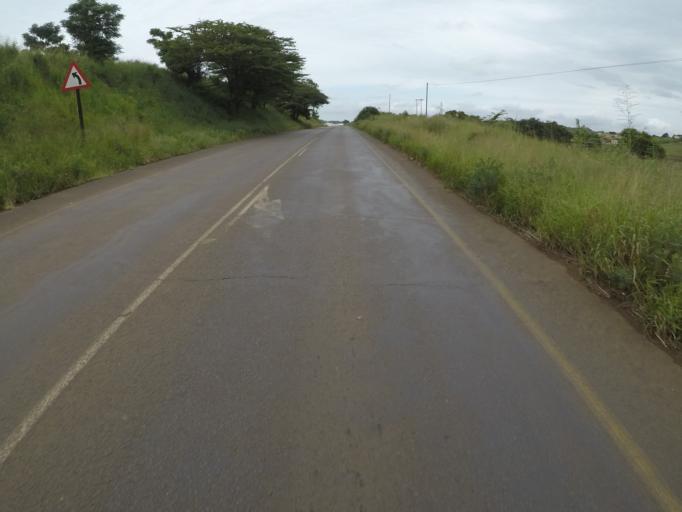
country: ZA
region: KwaZulu-Natal
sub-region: uThungulu District Municipality
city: Empangeni
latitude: -28.7675
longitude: 31.8759
